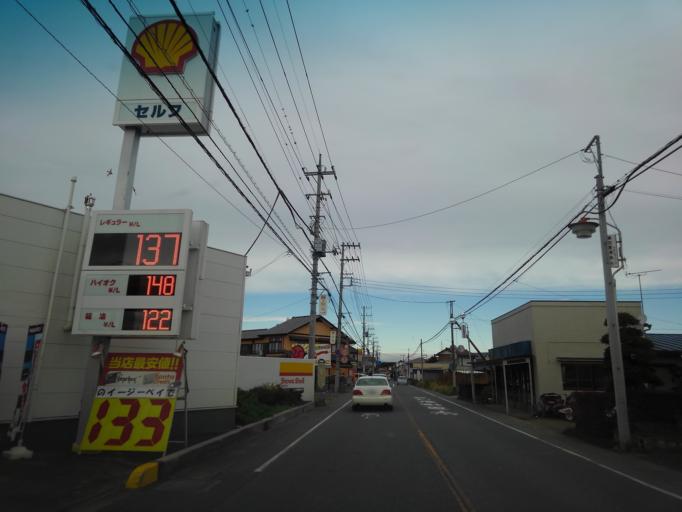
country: JP
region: Saitama
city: Morohongo
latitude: 35.9085
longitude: 139.3333
